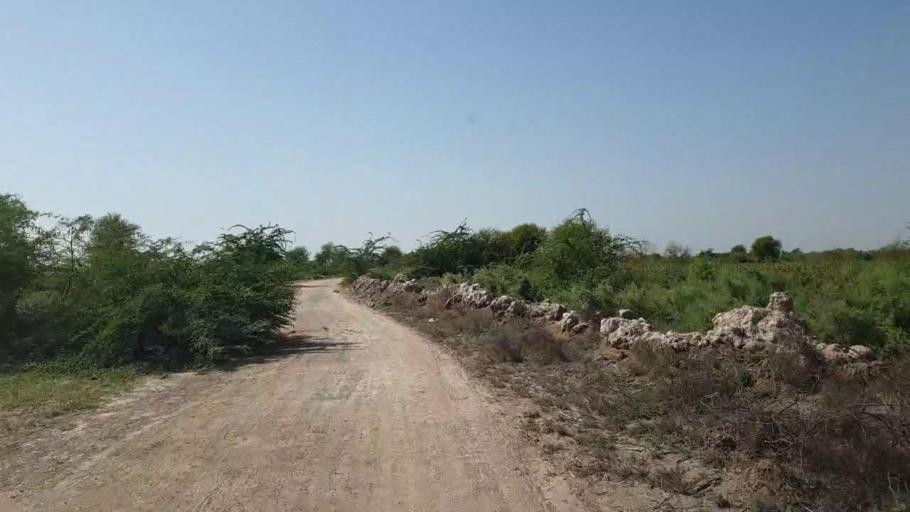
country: PK
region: Sindh
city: Tando Bago
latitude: 24.7063
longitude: 69.0540
